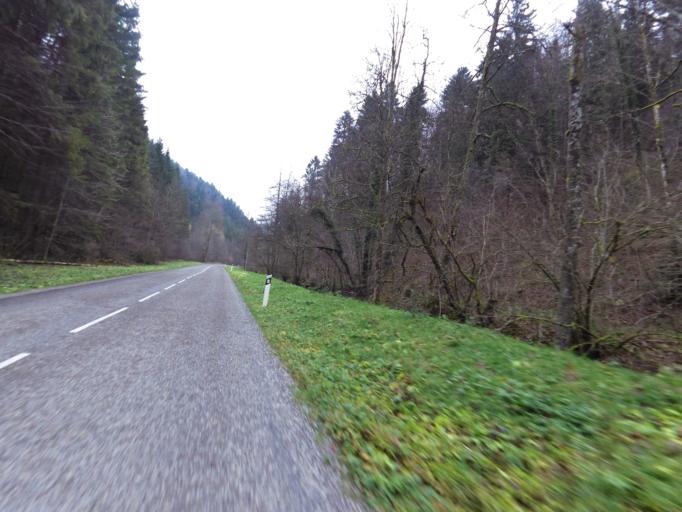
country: FR
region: Alsace
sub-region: Departement du Haut-Rhin
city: Ferrette
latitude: 47.4263
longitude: 7.2642
